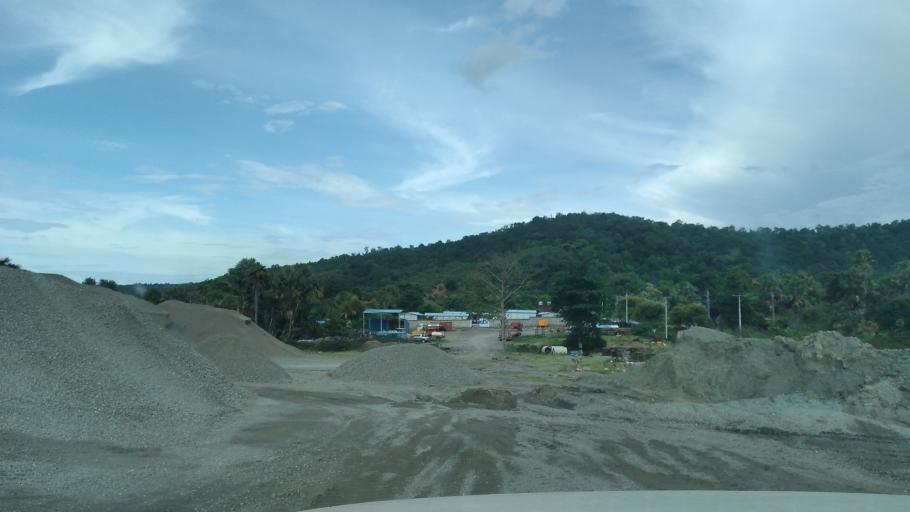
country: TL
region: Dili
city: Dili
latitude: -8.5986
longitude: 125.4781
